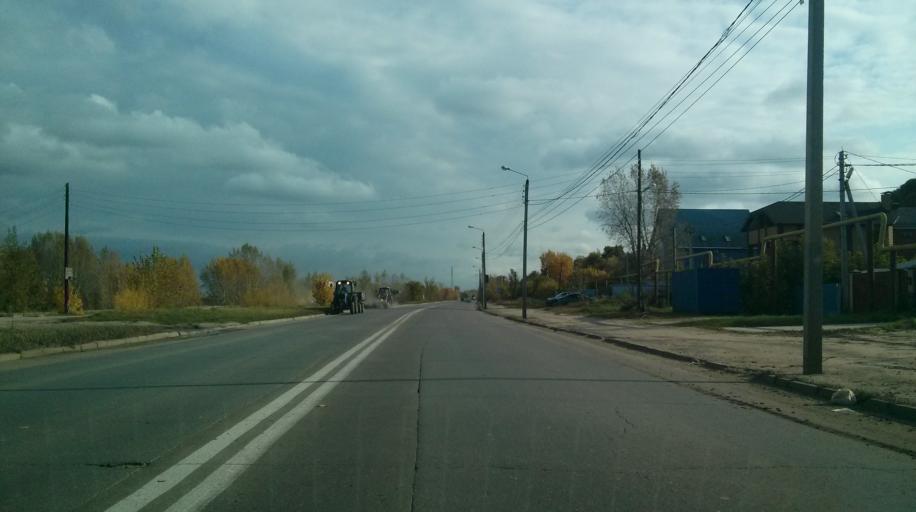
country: RU
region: Nizjnij Novgorod
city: Bor
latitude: 56.3113
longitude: 44.0899
